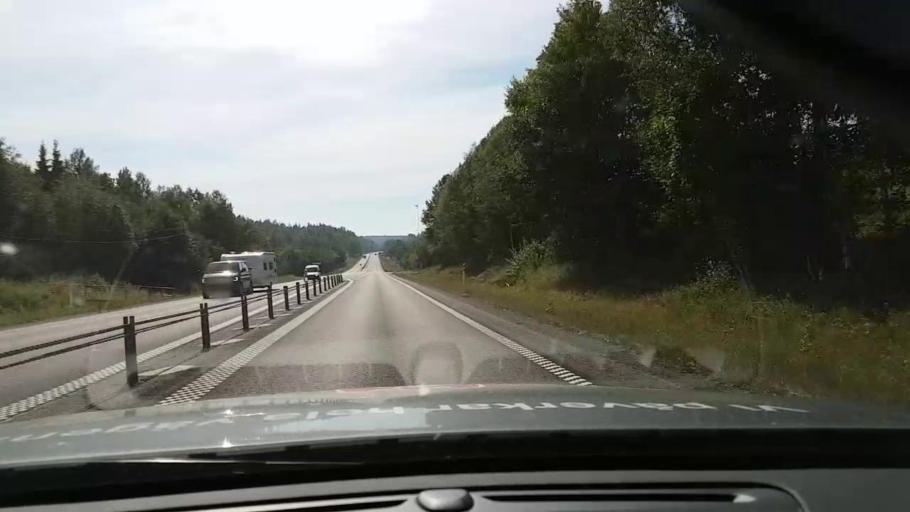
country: SE
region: Vaesternorrland
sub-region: OErnskoeldsviks Kommun
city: Husum
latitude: 63.3635
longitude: 19.1798
